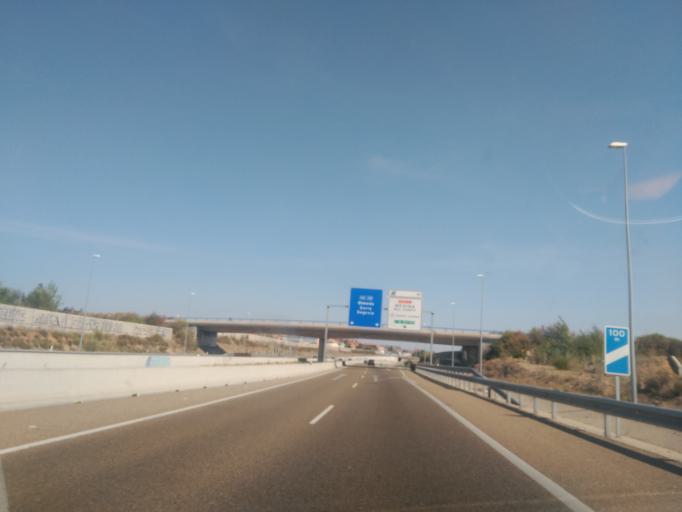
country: ES
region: Castille and Leon
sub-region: Provincia de Valladolid
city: Arroyo
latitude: 41.6082
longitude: -4.7607
